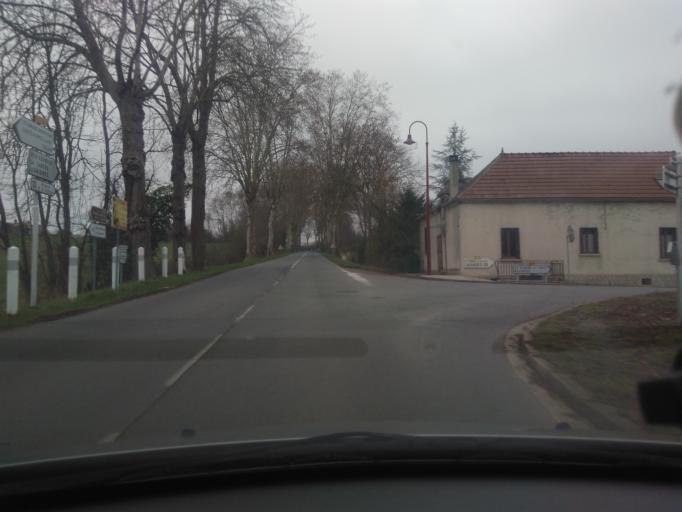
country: FR
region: Centre
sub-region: Departement du Cher
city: Le Chatelet
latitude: 46.6437
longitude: 2.2774
